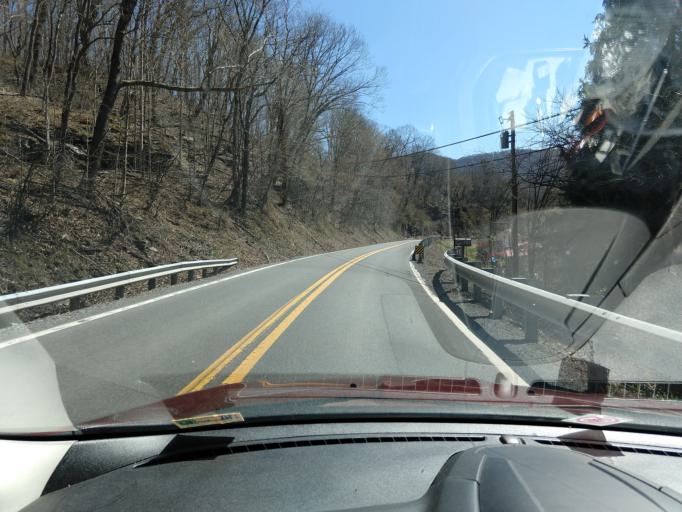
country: US
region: West Virginia
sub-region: Summers County
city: Hinton
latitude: 37.7766
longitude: -80.8909
